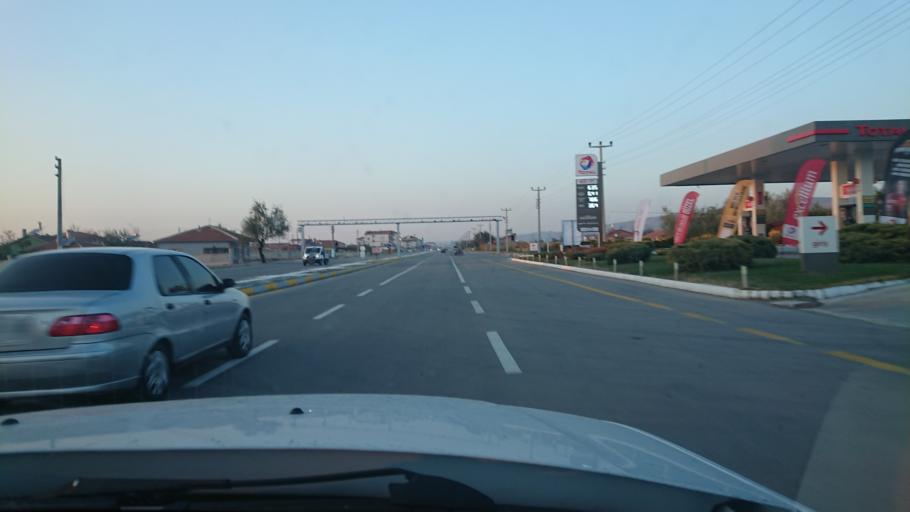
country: TR
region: Aksaray
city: Aksaray
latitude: 38.3321
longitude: 34.0502
